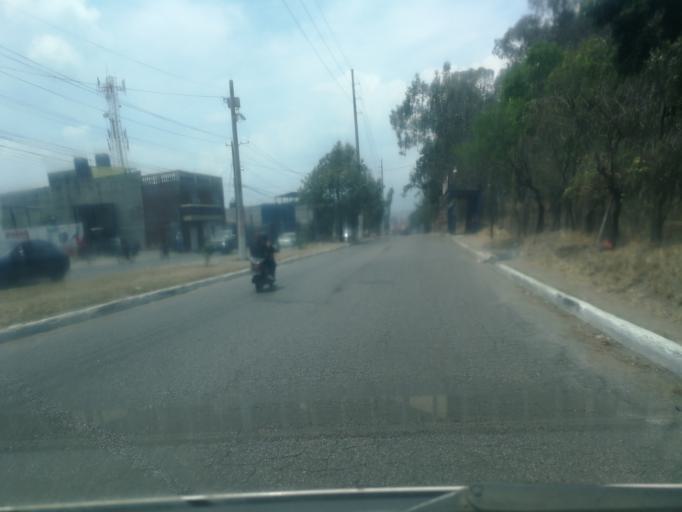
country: GT
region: Guatemala
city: Petapa
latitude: 14.5303
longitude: -90.5544
